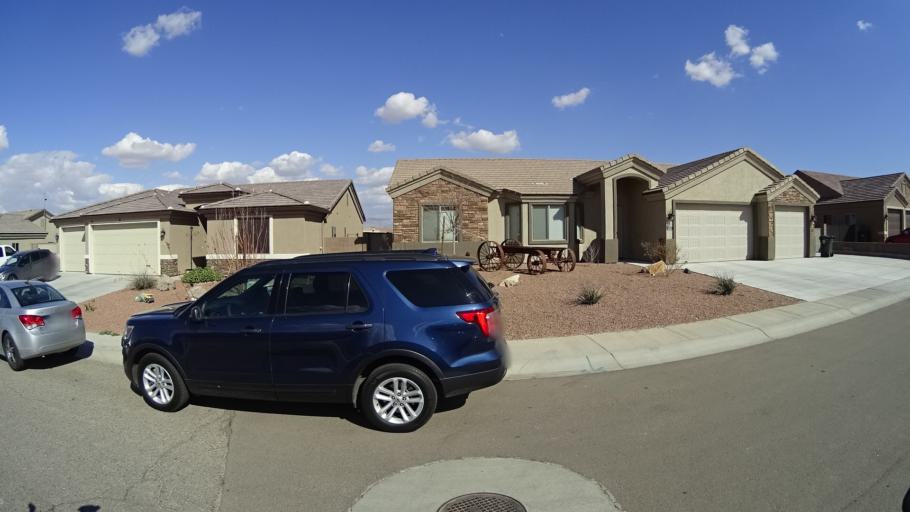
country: US
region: Arizona
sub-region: Mohave County
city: New Kingman-Butler
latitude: 35.2193
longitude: -113.9699
